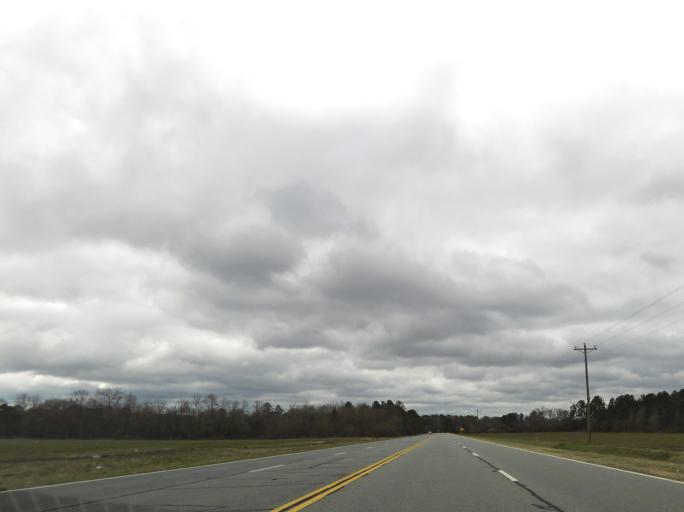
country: US
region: Georgia
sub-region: Bleckley County
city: Cochran
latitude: 32.4417
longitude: -83.3779
